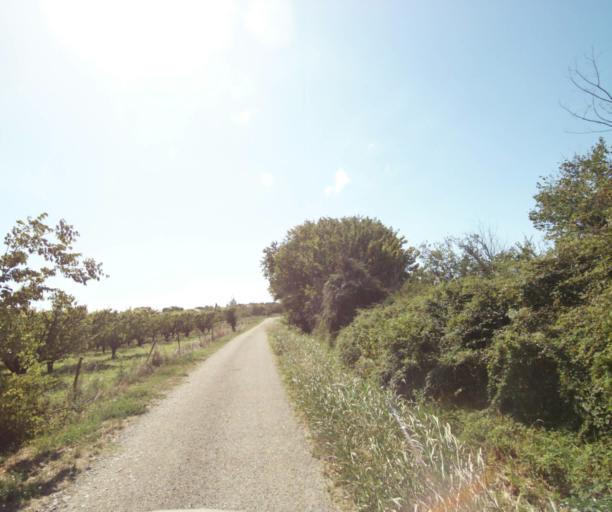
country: FR
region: Languedoc-Roussillon
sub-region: Departement du Gard
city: Bouillargues
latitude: 43.8075
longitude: 4.4255
